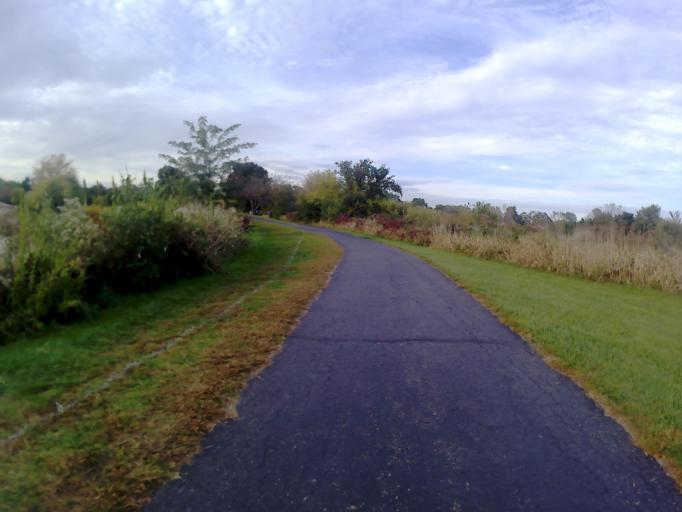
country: US
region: Illinois
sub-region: DuPage County
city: Lisle
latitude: 41.7938
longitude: -88.0796
